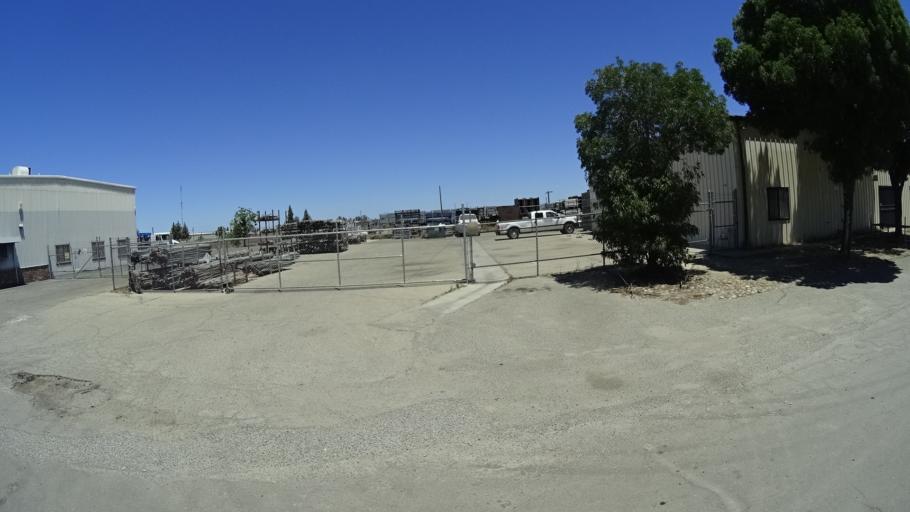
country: US
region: California
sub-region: Fresno County
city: Fresno
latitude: 36.6988
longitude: -119.7381
